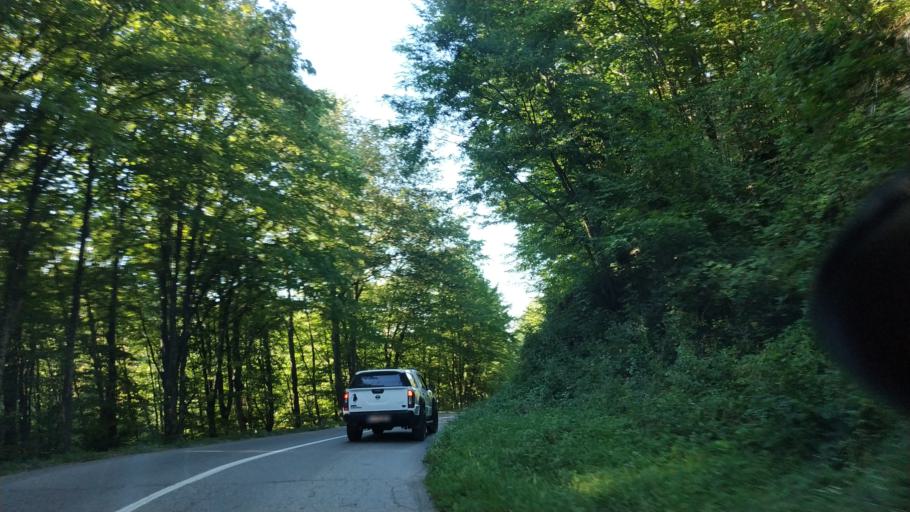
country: RS
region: Central Serbia
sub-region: Rasinski Okrug
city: Krusevac
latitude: 43.4566
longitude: 21.3591
